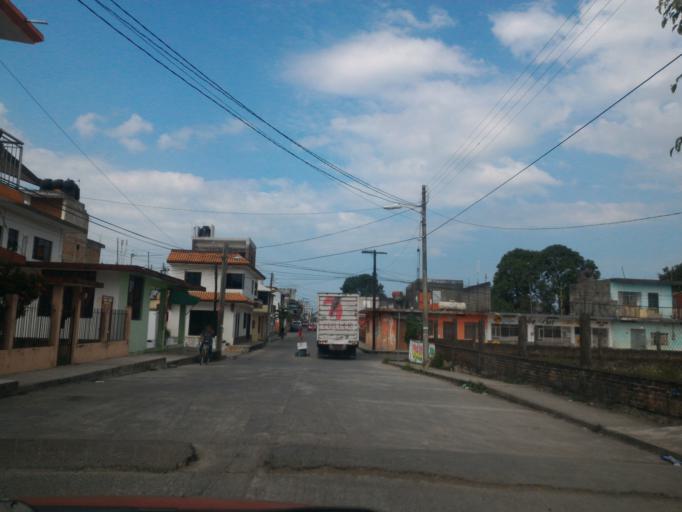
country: MX
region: Veracruz
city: San Rafael
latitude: 20.1854
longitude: -96.8674
